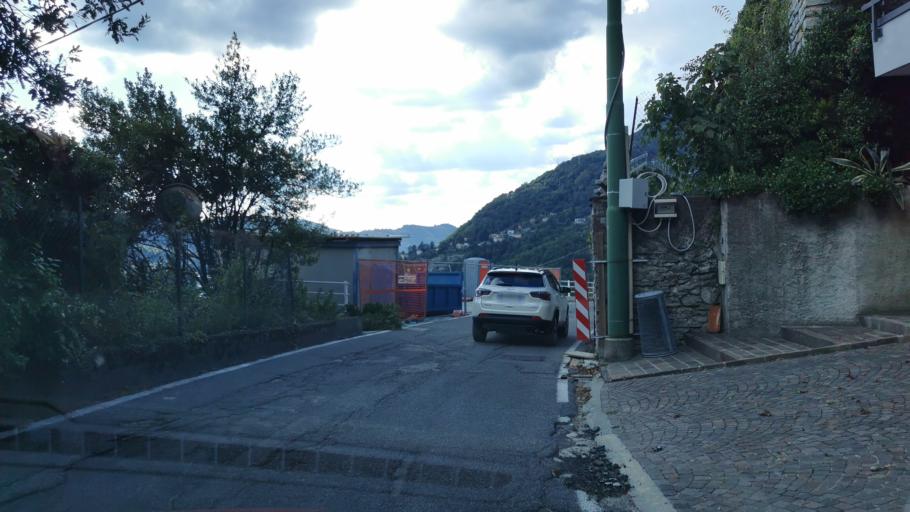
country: IT
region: Lombardy
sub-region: Provincia di Como
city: Cernobbio
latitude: 45.8491
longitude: 9.0834
